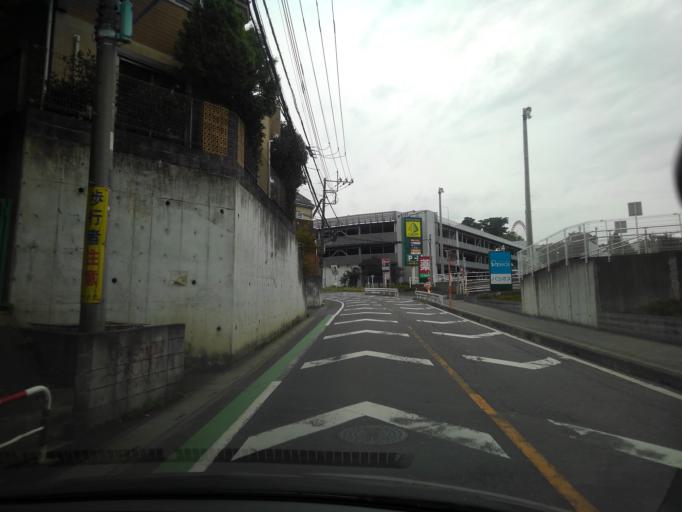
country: JP
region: Tokyo
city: Higashimurayama-shi
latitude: 35.7699
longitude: 139.4503
